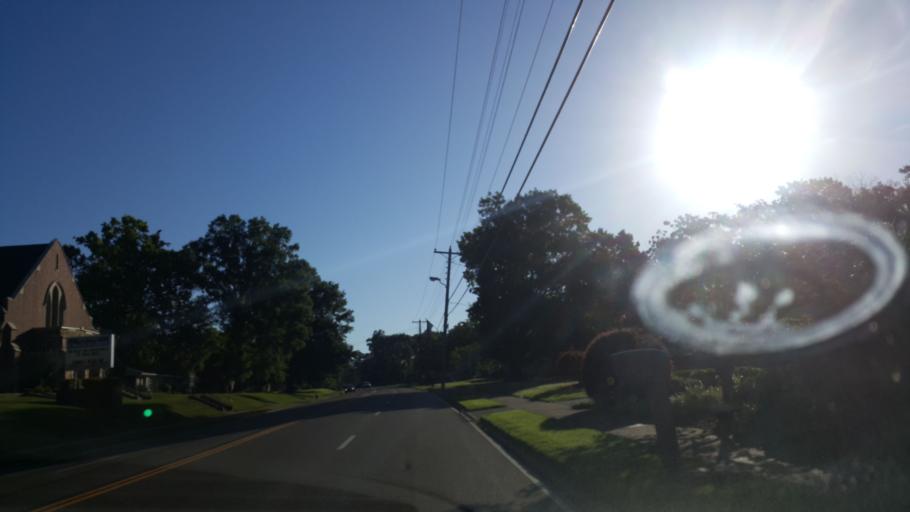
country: US
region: Tennessee
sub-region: Henderson County
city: Lexington
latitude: 35.6529
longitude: -88.3906
